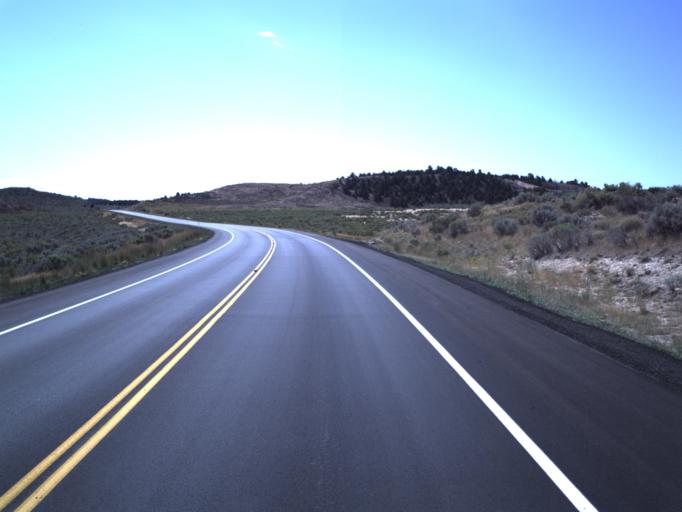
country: US
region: Utah
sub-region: Utah County
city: Eagle Mountain
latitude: 40.0024
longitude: -112.2753
